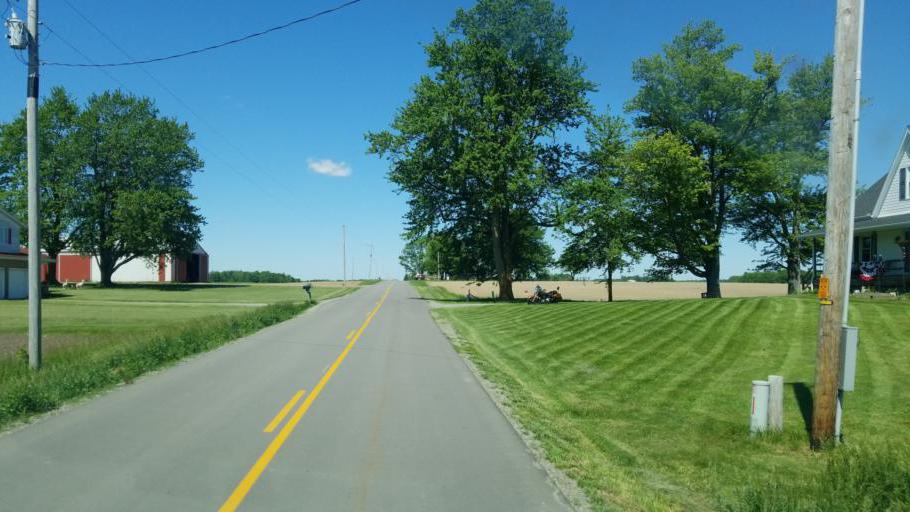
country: US
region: Ohio
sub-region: Logan County
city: Lakeview
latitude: 40.4174
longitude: -83.9573
